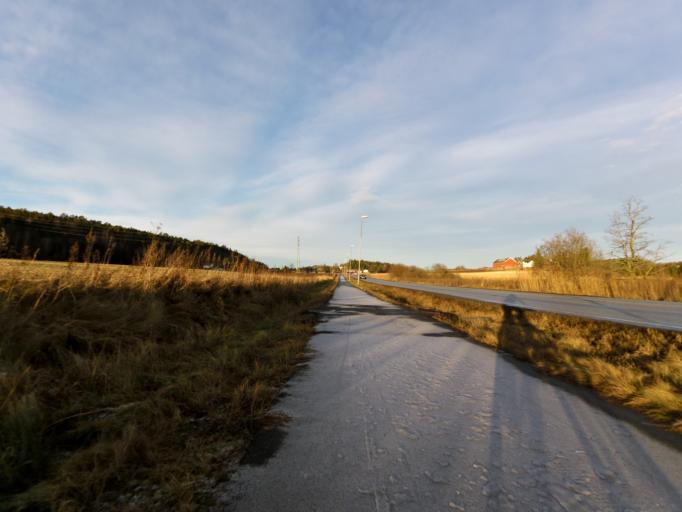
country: NO
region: Ostfold
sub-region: Fredrikstad
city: Fredrikstad
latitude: 59.2371
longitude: 10.9011
